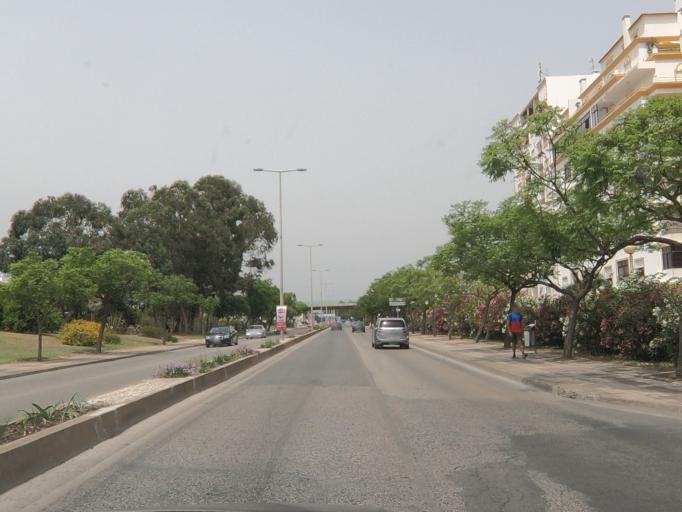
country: PT
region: Faro
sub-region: Portimao
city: Portimao
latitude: 37.1352
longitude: -8.5455
